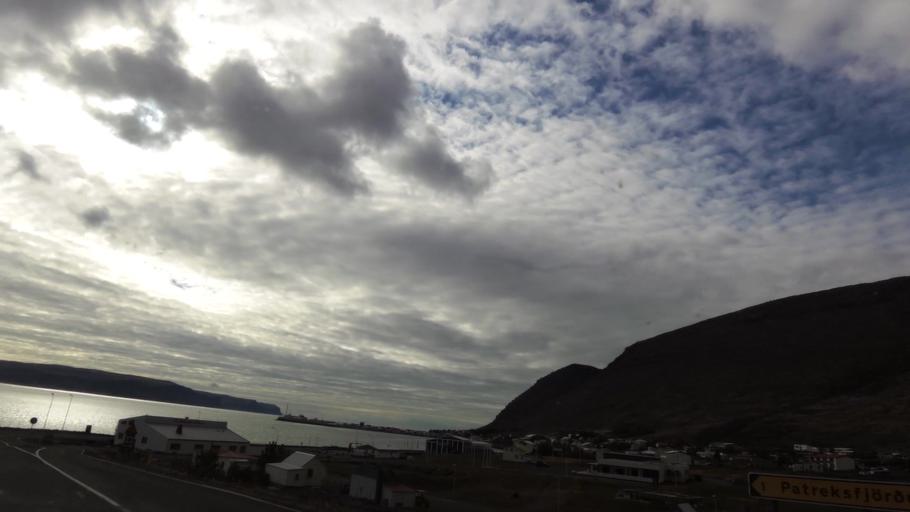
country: IS
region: West
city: Olafsvik
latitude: 65.5900
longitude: -23.9719
